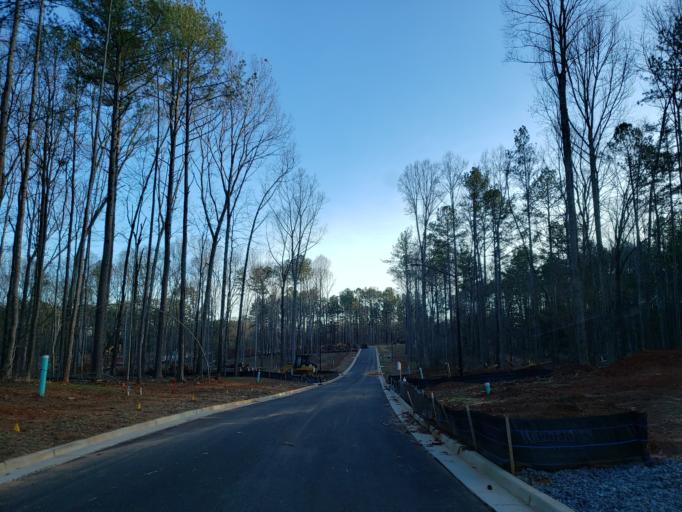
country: US
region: Georgia
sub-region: Cobb County
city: Acworth
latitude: 34.0292
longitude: -84.7311
